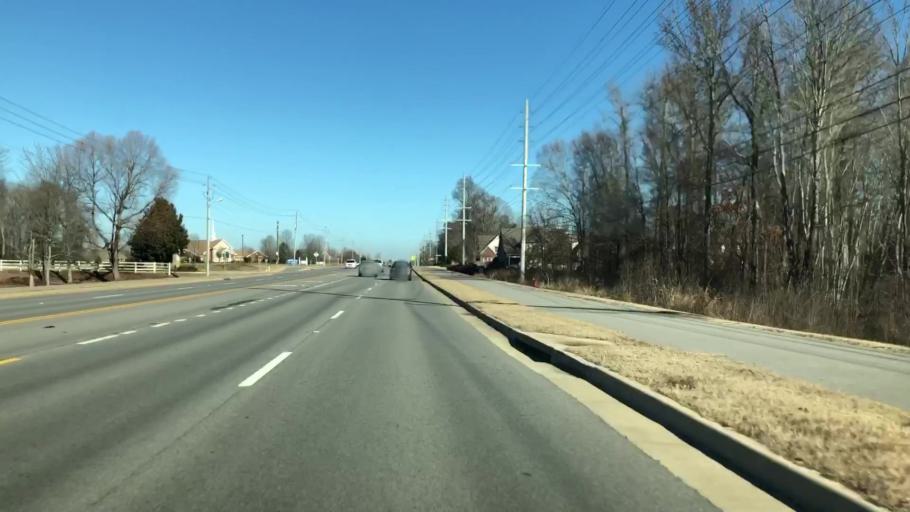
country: US
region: Alabama
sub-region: Madison County
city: Madison
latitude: 34.7156
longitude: -86.7864
